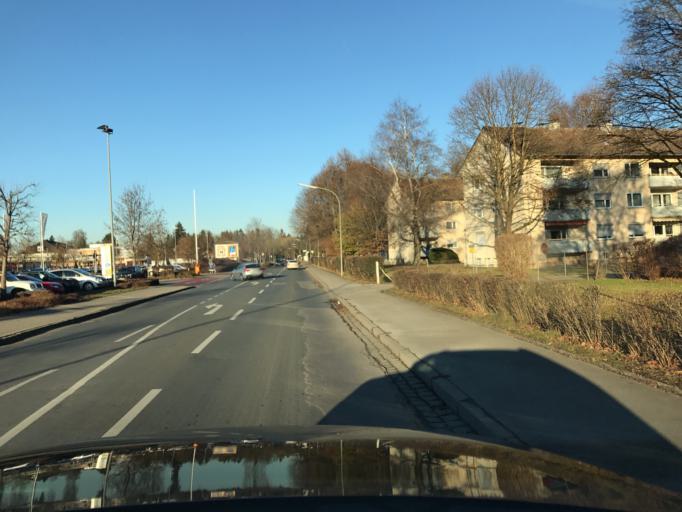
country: DE
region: Bavaria
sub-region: Upper Bavaria
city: Bad Aibling
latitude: 47.8675
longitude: 12.0012
